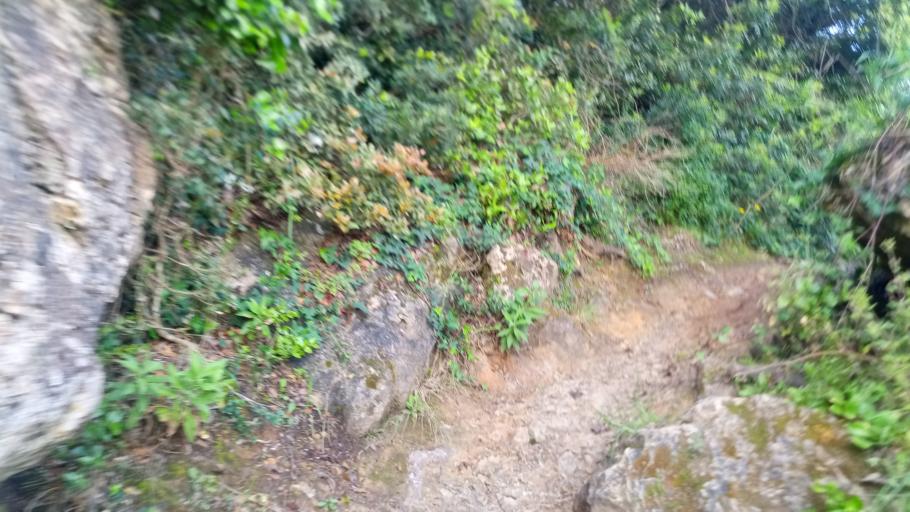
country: PT
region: Leiria
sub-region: Caldas da Rainha
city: Caldas da Rainha
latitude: 39.4024
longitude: -9.1904
